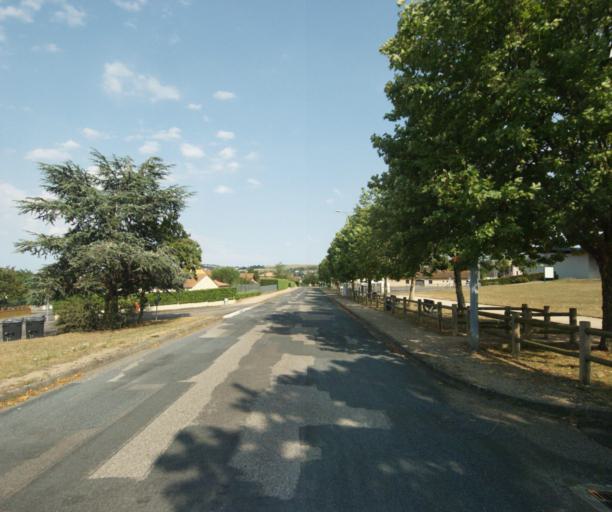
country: FR
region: Rhone-Alpes
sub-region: Departement du Rhone
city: Saint-Germain-Nuelles
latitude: 45.8337
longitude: 4.6047
